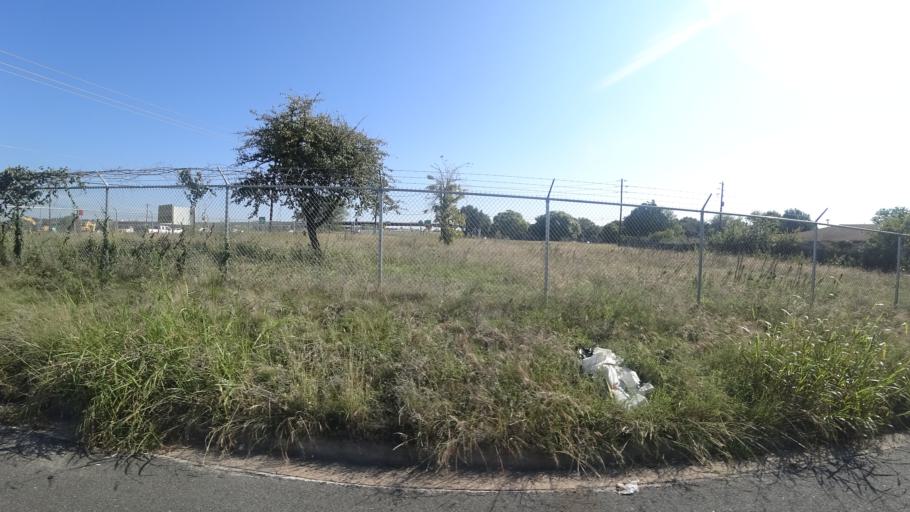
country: US
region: Texas
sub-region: Travis County
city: Austin
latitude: 30.3234
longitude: -97.6776
